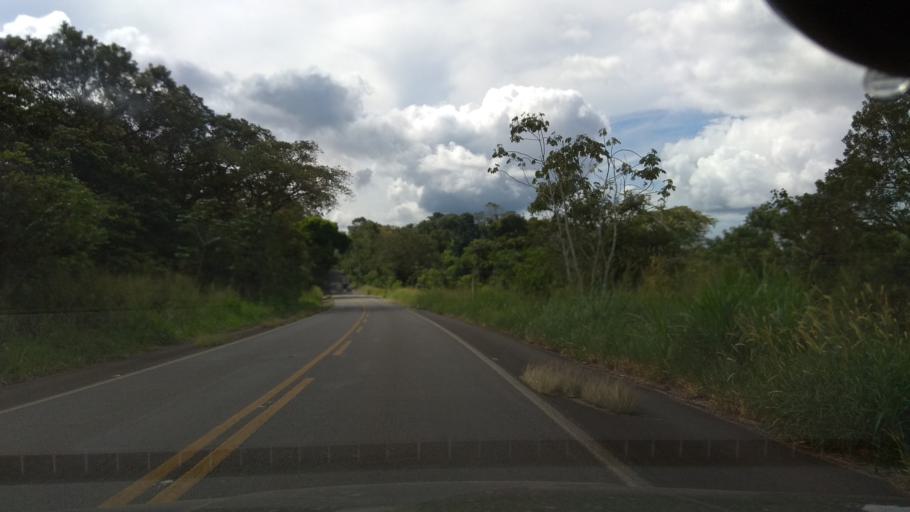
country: BR
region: Bahia
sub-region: Itajuipe
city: Itajuipe
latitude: -14.6347
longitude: -39.3356
